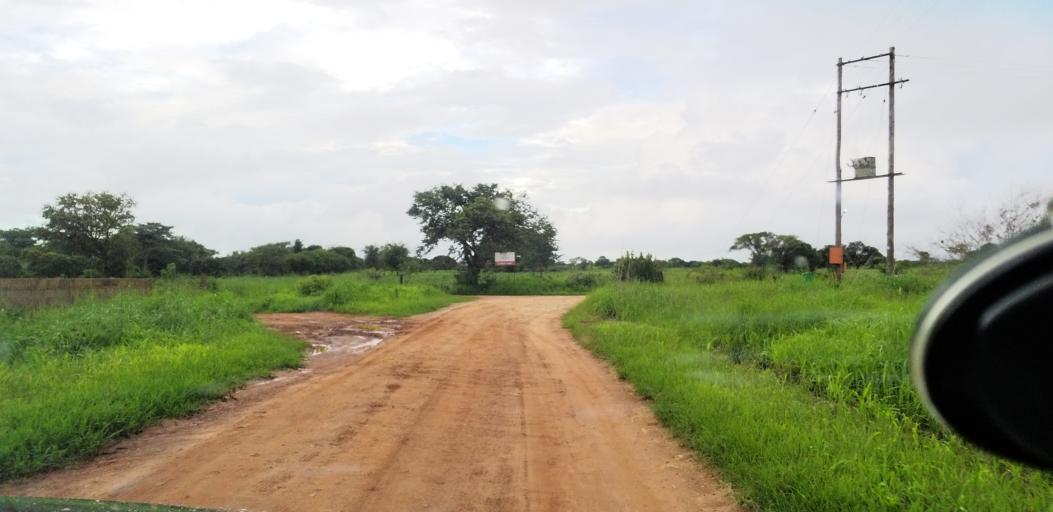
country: ZM
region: Lusaka
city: Lusaka
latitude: -15.5243
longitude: 28.3099
